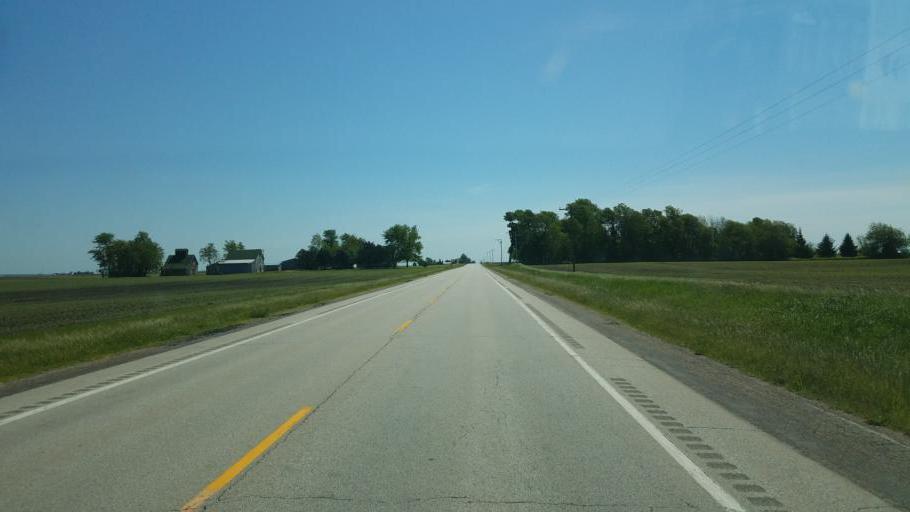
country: US
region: Illinois
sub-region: McLean County
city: Heyworth
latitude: 40.3123
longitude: -88.9172
